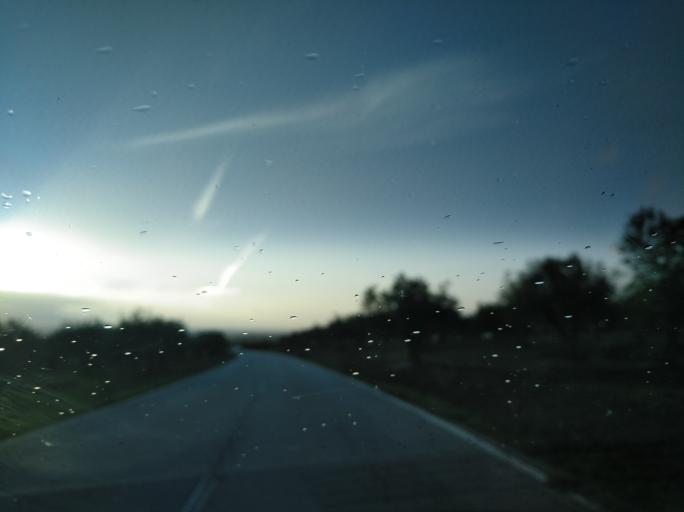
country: PT
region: Portalegre
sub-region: Campo Maior
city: Campo Maior
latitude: 39.0096
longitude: -7.1074
